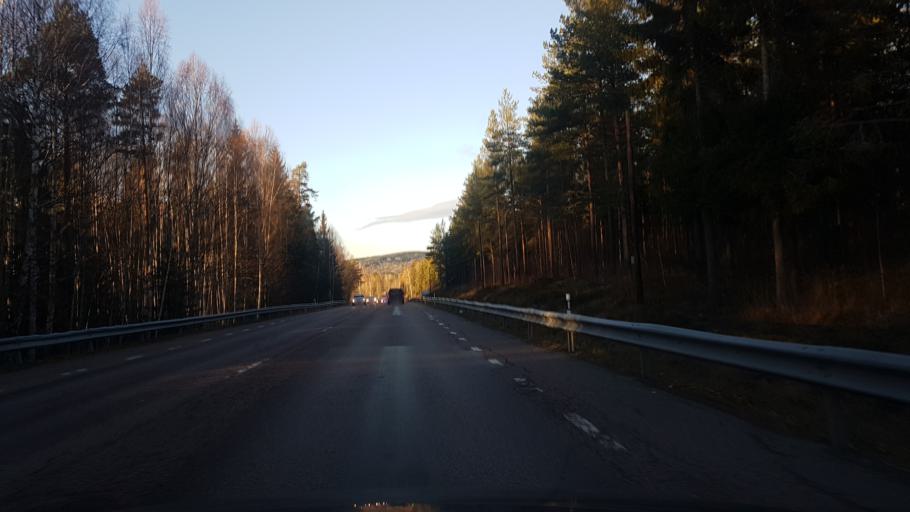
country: SE
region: Dalarna
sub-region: Faluns Kommun
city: Bjursas
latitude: 60.7114
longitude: 15.4622
